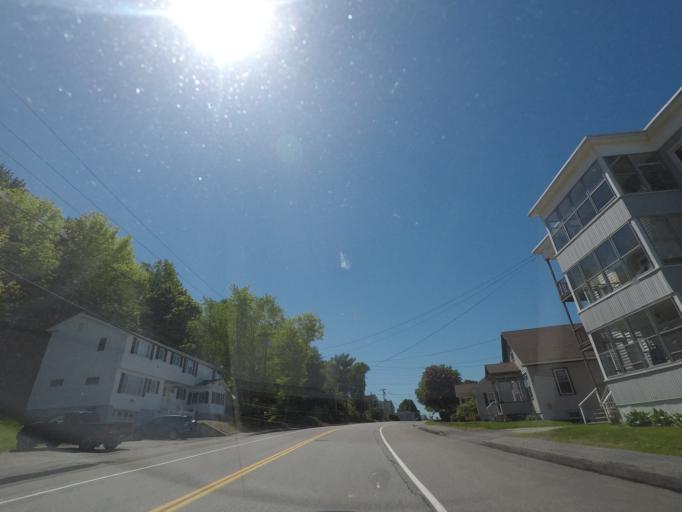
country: US
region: Maine
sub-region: Kennebec County
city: Augusta
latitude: 44.3321
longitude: -69.7768
